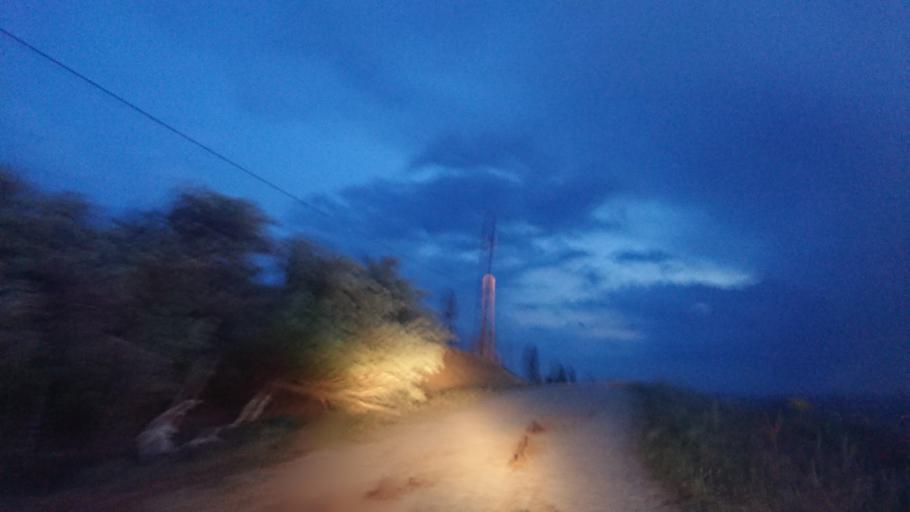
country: TR
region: Aksaray
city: Ortakoy
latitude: 38.6338
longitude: 34.0148
